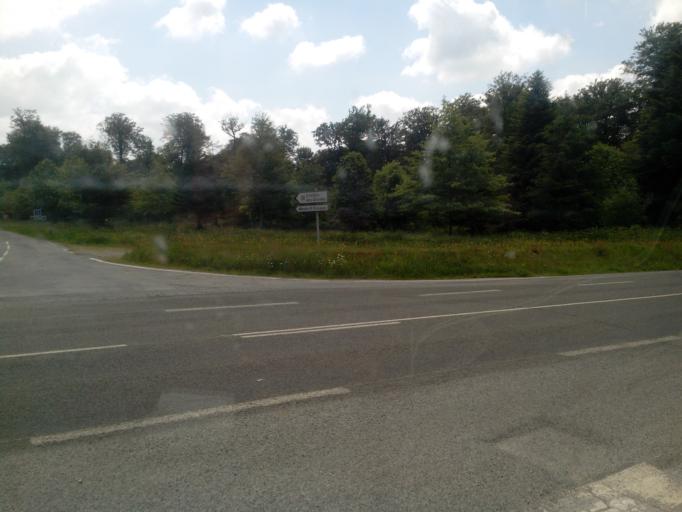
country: FR
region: Brittany
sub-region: Departement d'Ille-et-Vilaine
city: Landean
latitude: 48.3937
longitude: -1.1640
